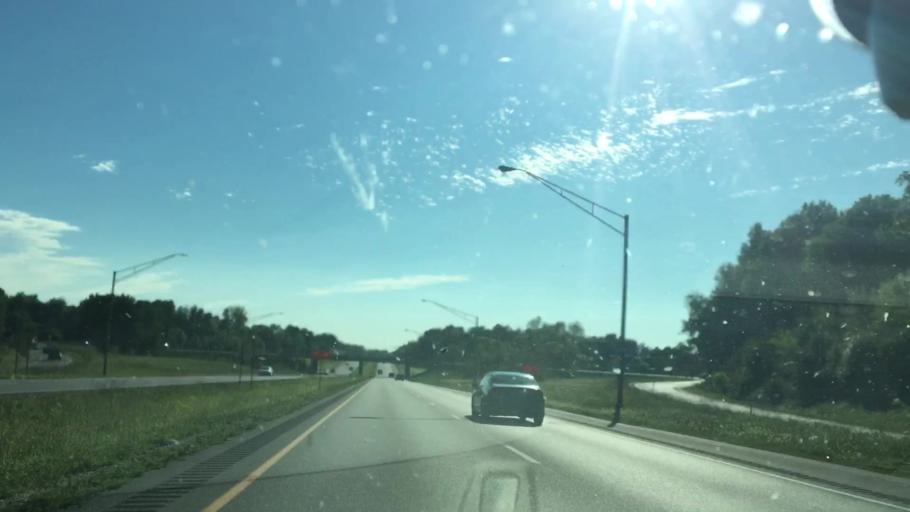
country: US
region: Kentucky
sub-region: Daviess County
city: Owensboro
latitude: 37.7335
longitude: -87.0853
